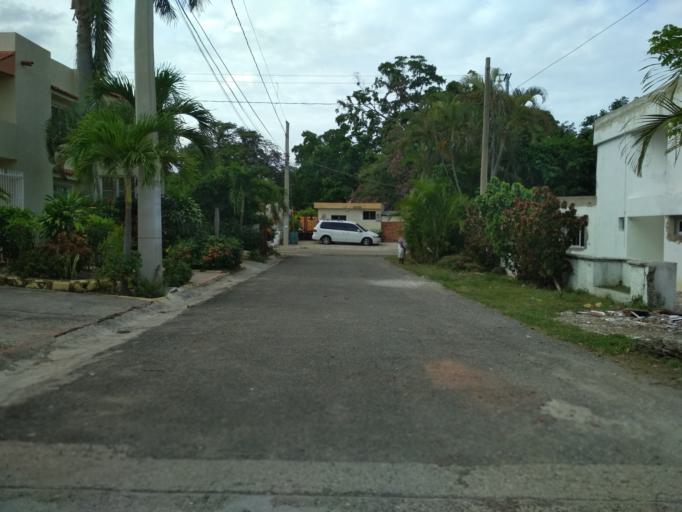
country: DO
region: Puerto Plata
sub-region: Puerto Plata
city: Puerto Plata
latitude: 19.8138
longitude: -70.7149
